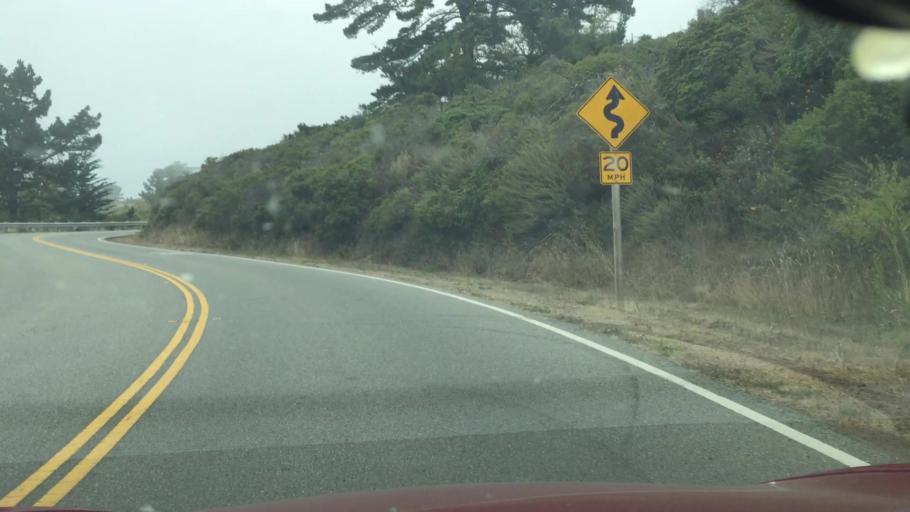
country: US
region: California
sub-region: Marin County
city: Sausalito
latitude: 37.8357
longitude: -122.4997
